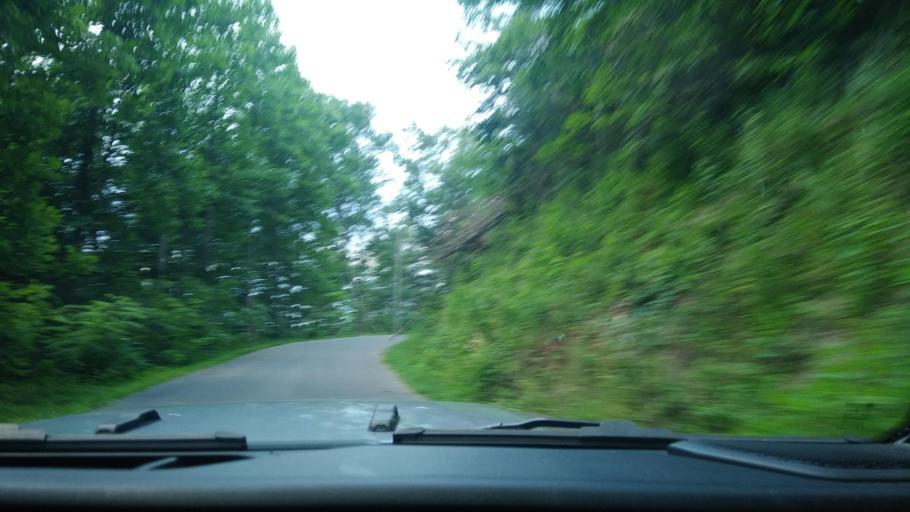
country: US
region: Tennessee
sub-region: Sevier County
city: Gatlinburg
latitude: 35.7402
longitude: -83.4820
